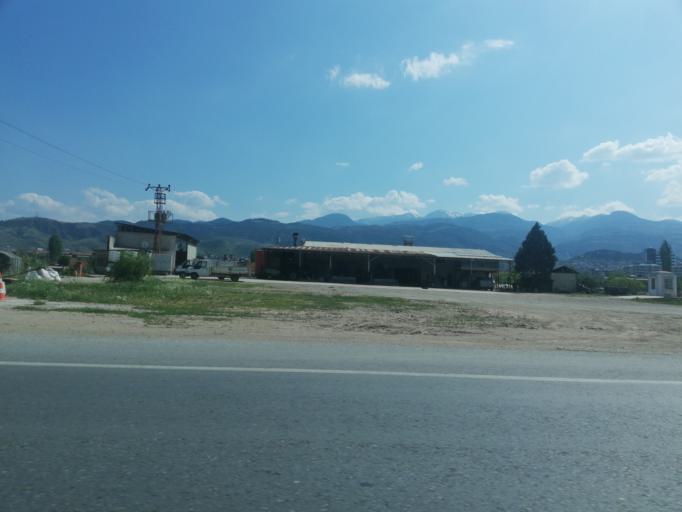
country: TR
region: Manisa
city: Alasehir
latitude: 38.3600
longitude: 28.5307
